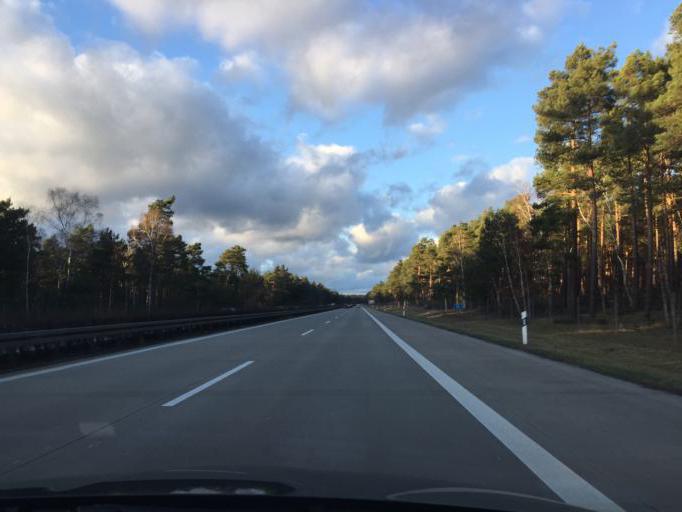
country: DE
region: Brandenburg
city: Halbe
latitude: 52.0417
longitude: 13.6669
